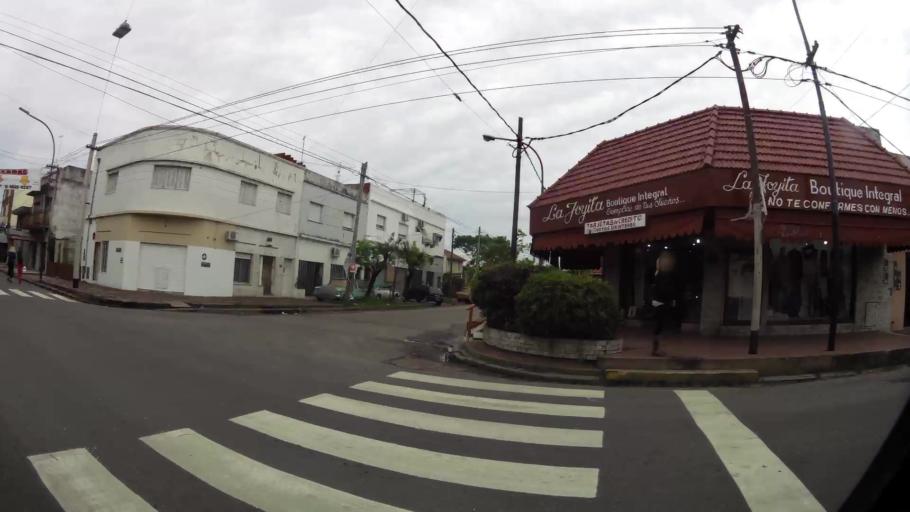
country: AR
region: Buenos Aires
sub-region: Partido de Lanus
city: Lanus
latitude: -34.7006
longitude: -58.3821
